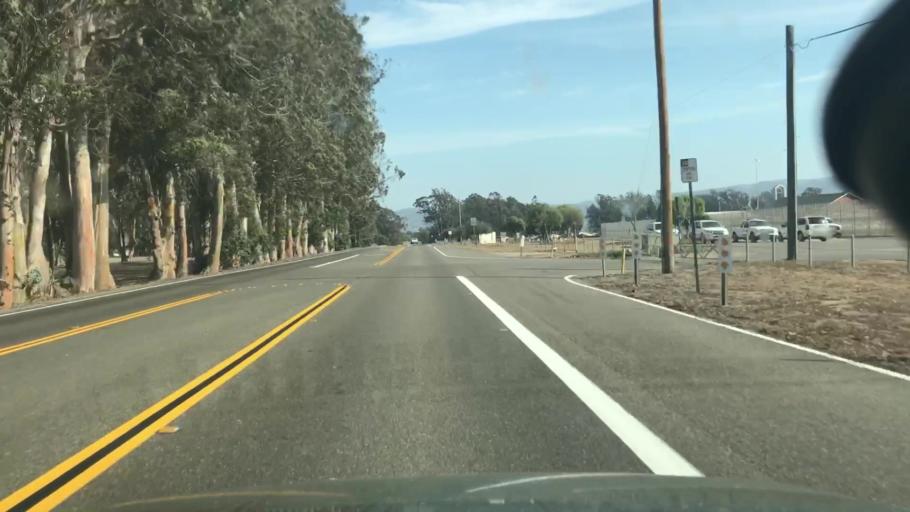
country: US
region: California
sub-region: Santa Barbara County
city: Vandenberg Village
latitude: 34.6797
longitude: -120.4984
